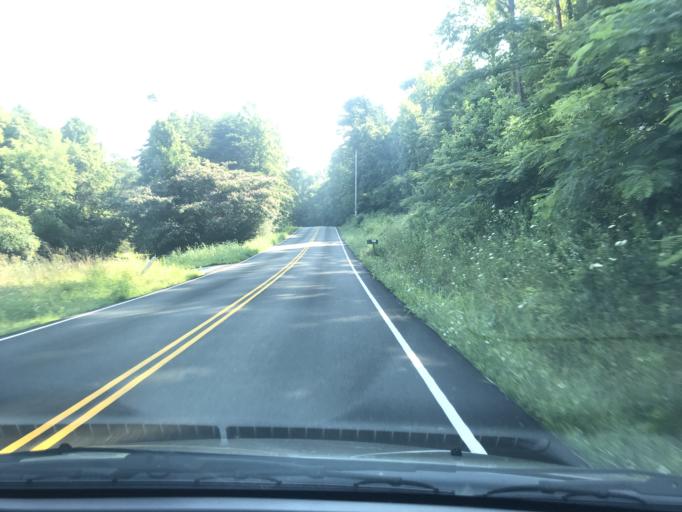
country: US
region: Tennessee
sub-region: Loudon County
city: Loudon
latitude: 35.8036
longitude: -84.3625
